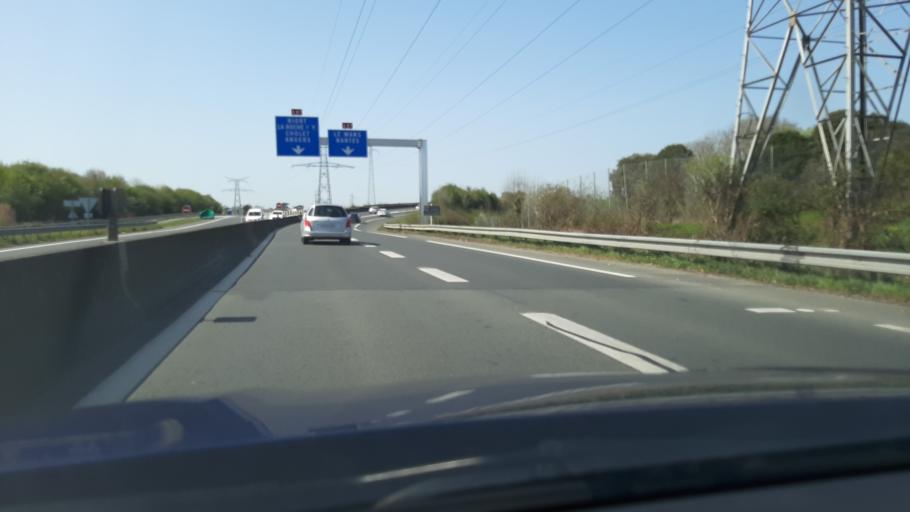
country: FR
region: Pays de la Loire
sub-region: Departement de Maine-et-Loire
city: Trelaze
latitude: 47.4711
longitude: -0.4999
